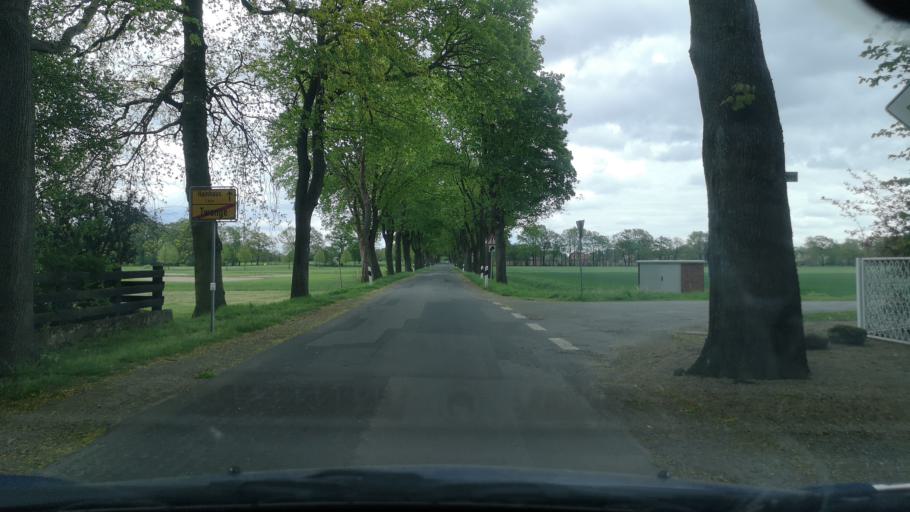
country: DE
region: Lower Saxony
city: Langenhagen
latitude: 52.4871
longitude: 9.7544
